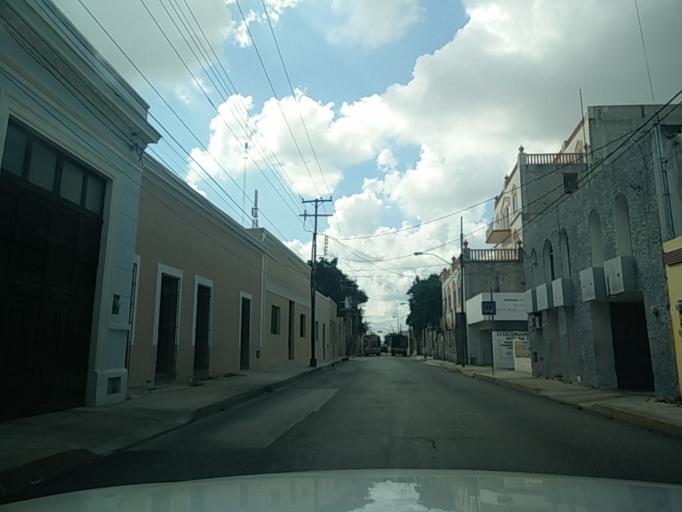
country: MX
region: Yucatan
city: Merida
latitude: 20.9822
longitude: -89.6220
